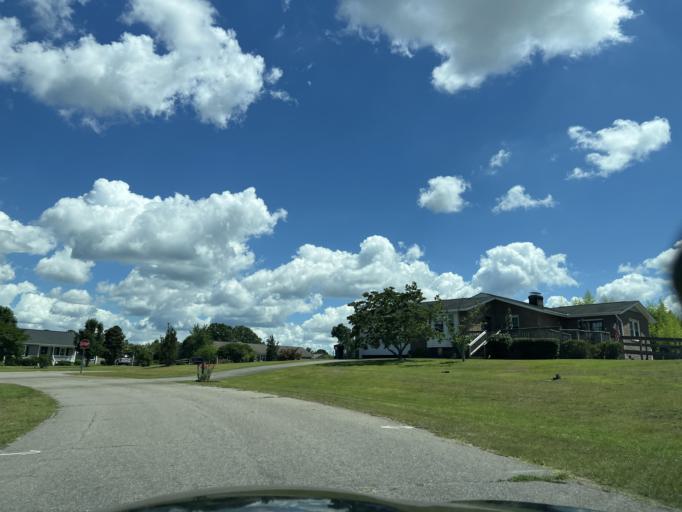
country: US
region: North Carolina
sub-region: Lee County
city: Sanford
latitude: 35.4319
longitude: -79.1605
